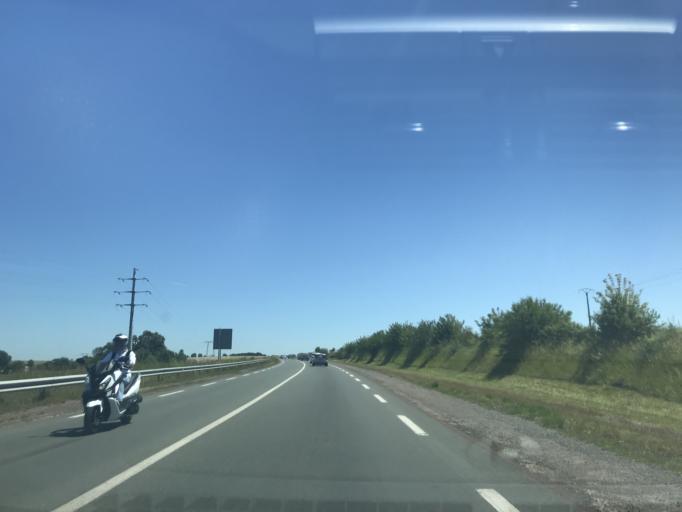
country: FR
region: Poitou-Charentes
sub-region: Departement de la Charente-Maritime
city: Saint-Georges-de-Didonne
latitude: 45.6150
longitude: -0.9863
